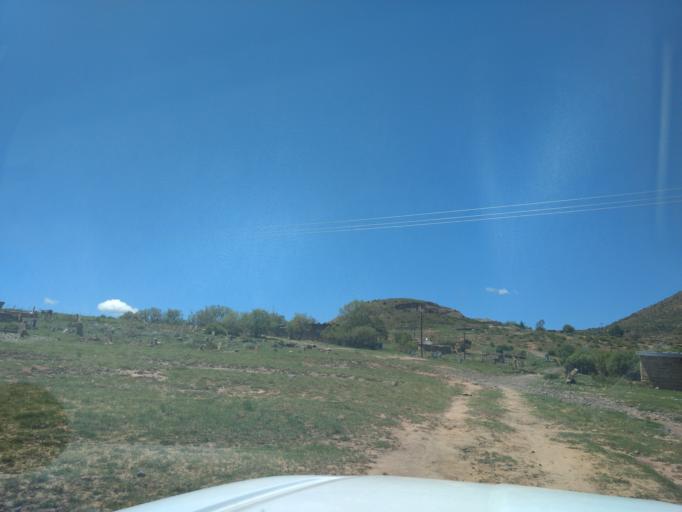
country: LS
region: Maseru
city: Maseru
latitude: -29.4577
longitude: 27.3731
